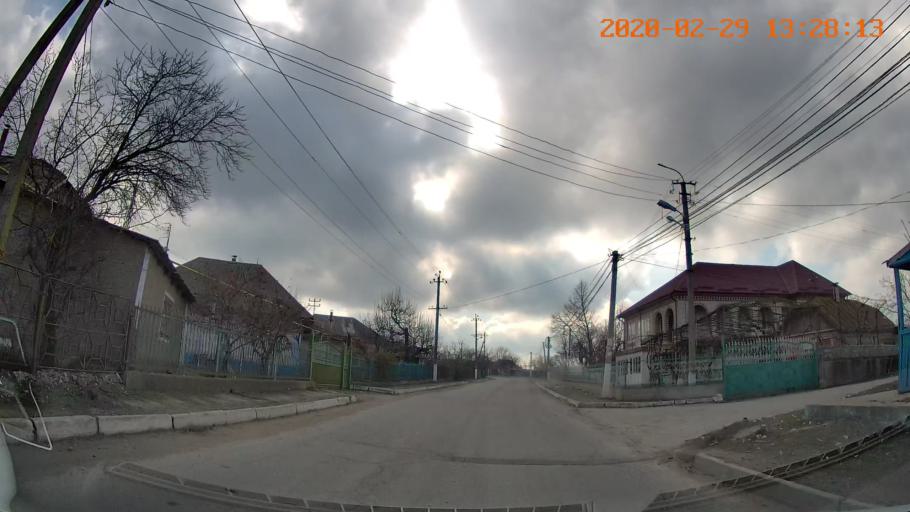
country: MD
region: Telenesti
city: Camenca
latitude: 47.9071
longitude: 28.6434
